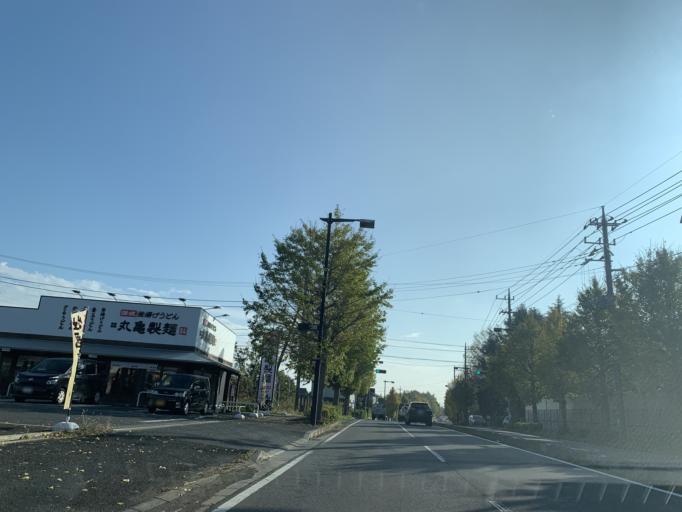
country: JP
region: Chiba
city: Nagareyama
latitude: 35.8624
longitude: 139.9121
